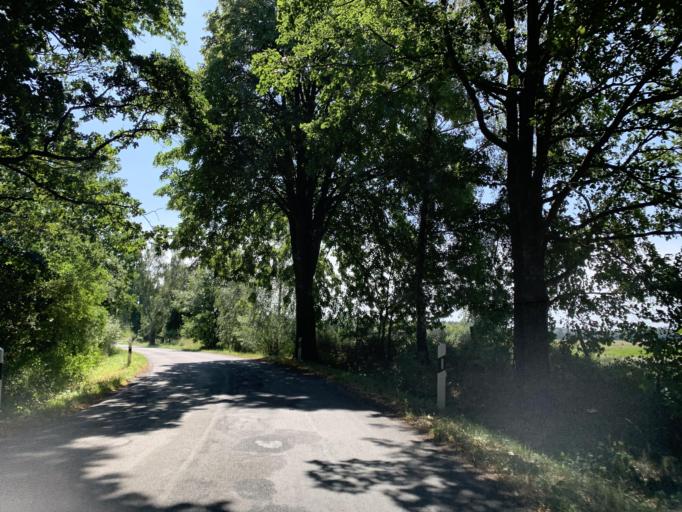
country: DE
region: Mecklenburg-Vorpommern
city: Carpin
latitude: 53.3292
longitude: 13.2405
